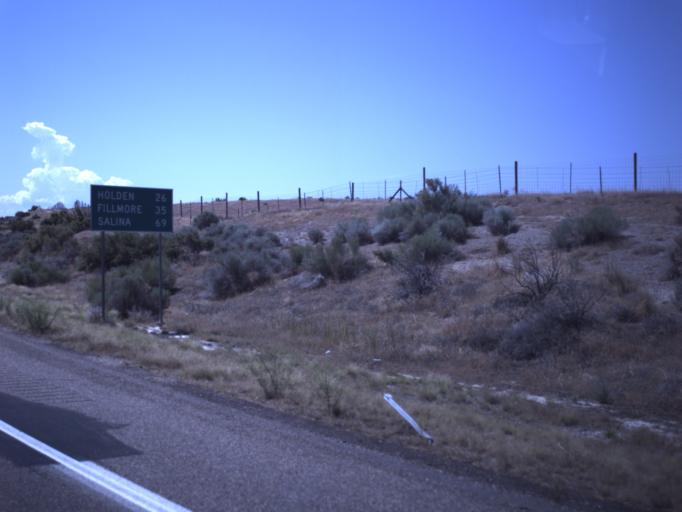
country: US
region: Utah
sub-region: Millard County
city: Delta
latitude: 39.3958
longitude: -112.5030
